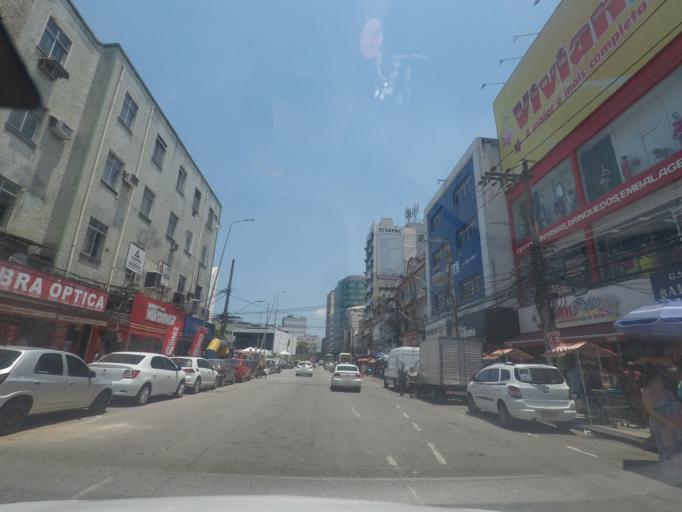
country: BR
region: Rio de Janeiro
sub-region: Duque De Caxias
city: Duque de Caxias
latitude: -22.7875
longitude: -43.3108
